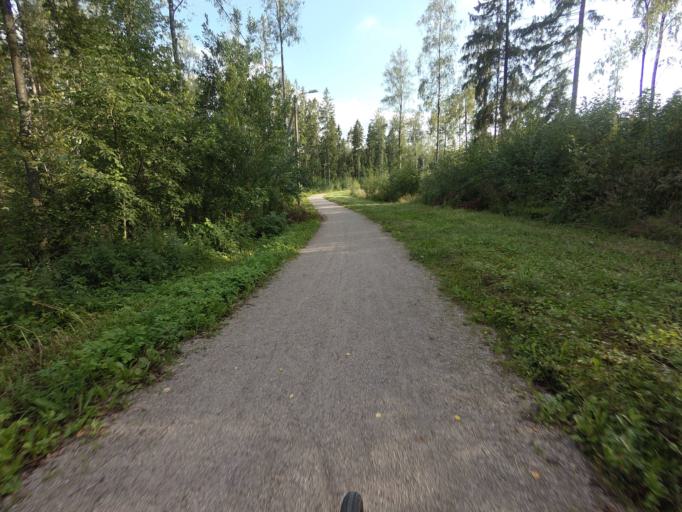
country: FI
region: Uusimaa
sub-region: Helsinki
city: Espoo
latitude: 60.1664
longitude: 24.6428
